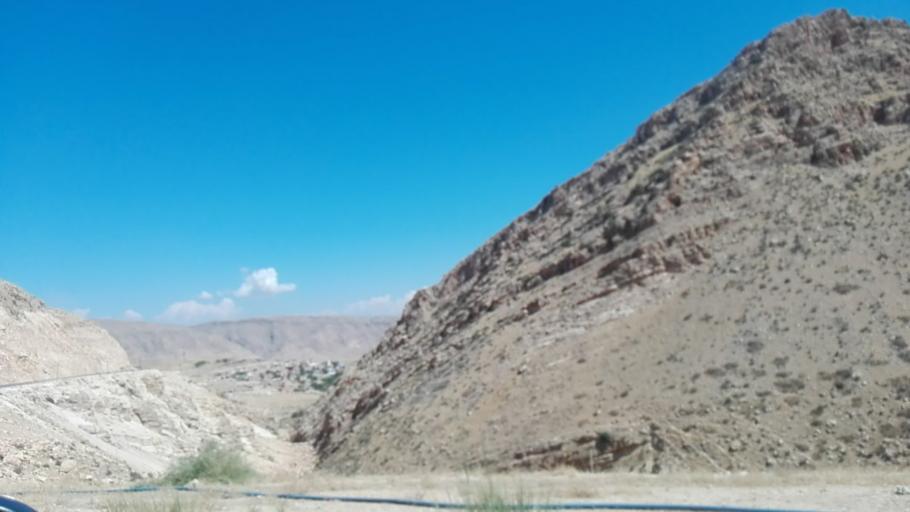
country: TR
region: Batman
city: Hasankeyf
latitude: 37.6976
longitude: 41.4583
